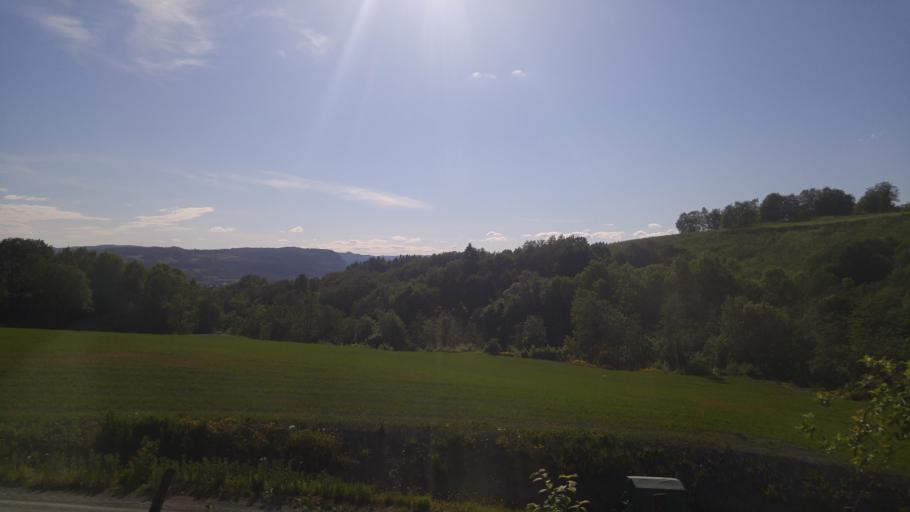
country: NO
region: Sor-Trondelag
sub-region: Melhus
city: Melhus
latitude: 63.3380
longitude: 10.3412
